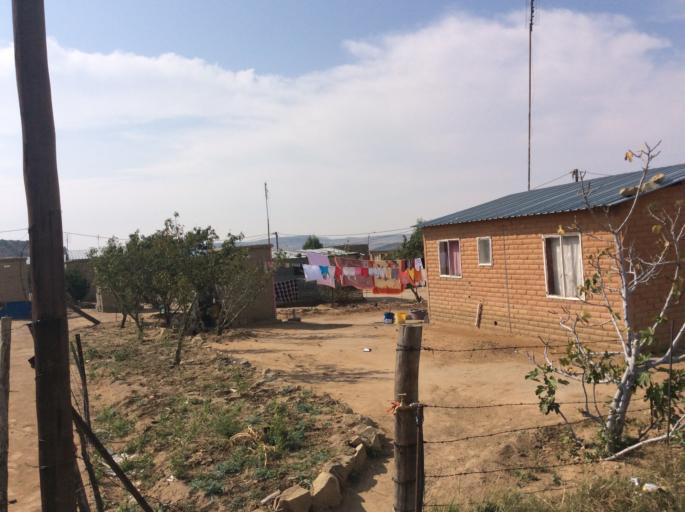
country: ZA
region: Orange Free State
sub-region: Xhariep District Municipality
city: Dewetsdorp
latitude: -29.5975
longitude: 26.6811
